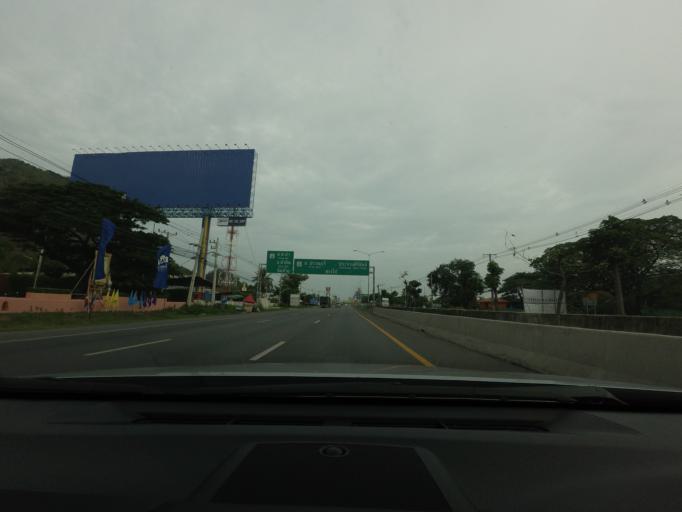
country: TH
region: Phetchaburi
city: Cha-am
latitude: 12.8231
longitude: 99.9381
